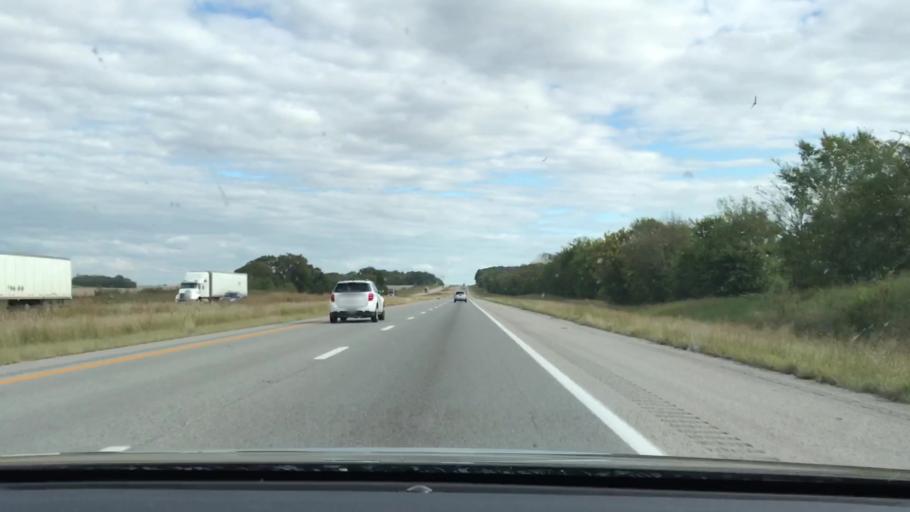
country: US
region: Kentucky
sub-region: Christian County
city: Hopkinsville
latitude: 36.7855
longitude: -87.5821
